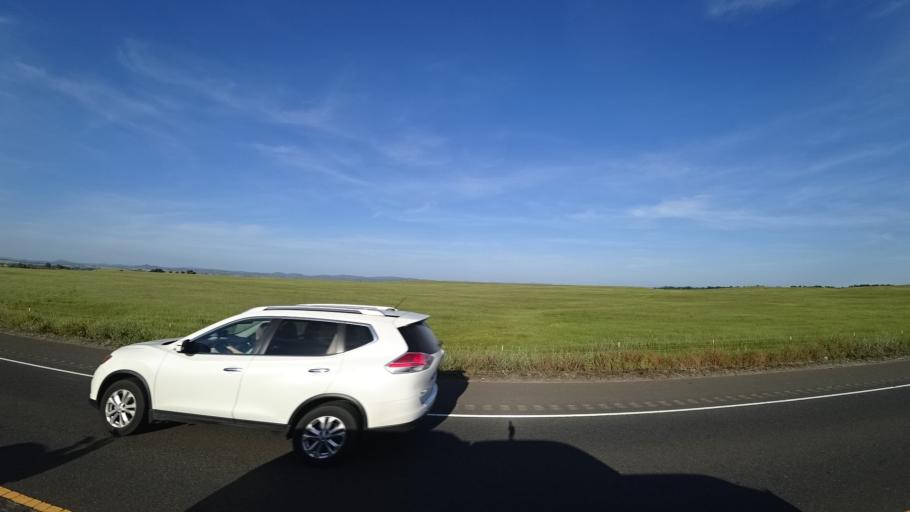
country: US
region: California
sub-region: Placer County
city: Sheridan
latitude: 38.9488
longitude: -121.3558
